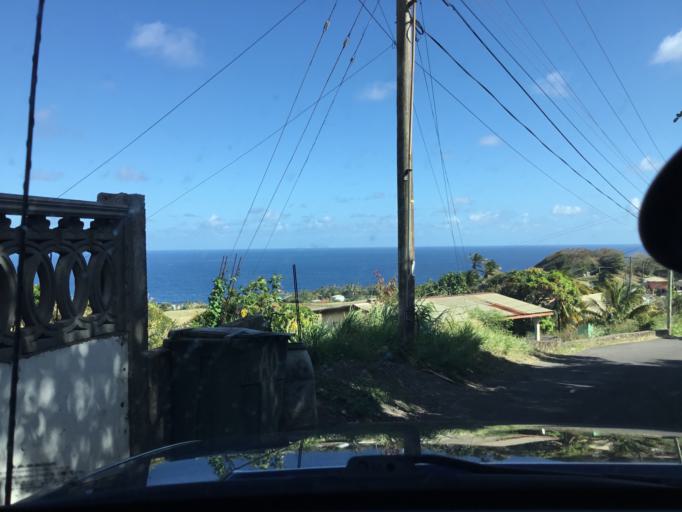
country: VC
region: Charlotte
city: Biabou
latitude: 13.1539
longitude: -61.1557
